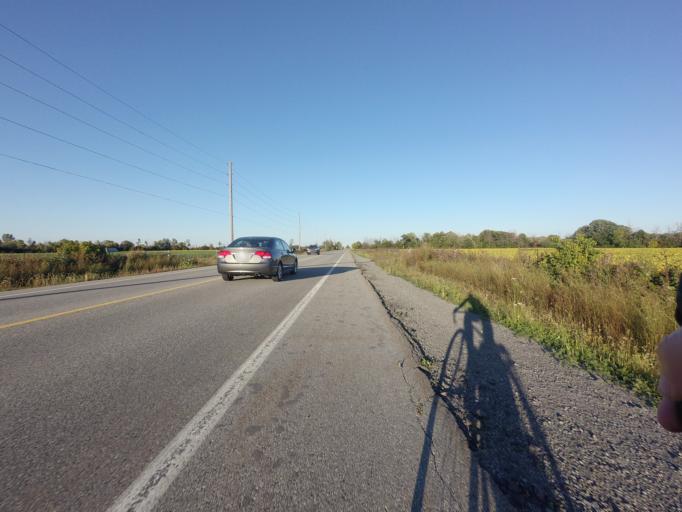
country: CA
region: Ontario
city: Bells Corners
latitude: 45.2943
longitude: -75.7211
